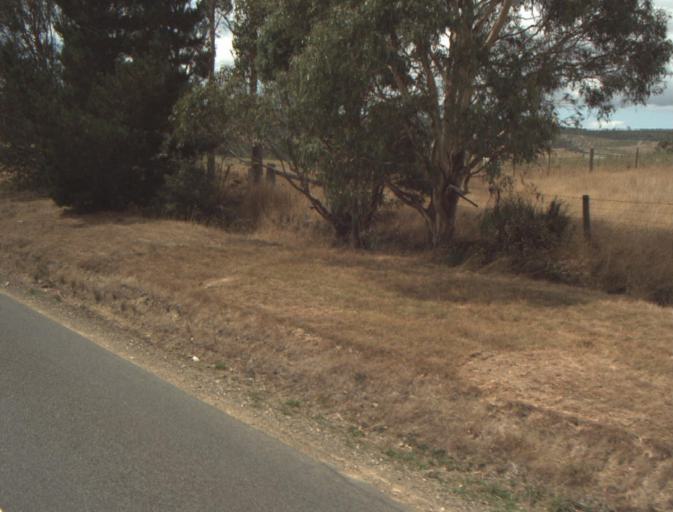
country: AU
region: Tasmania
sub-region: Launceston
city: Mayfield
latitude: -41.2132
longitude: 147.1211
